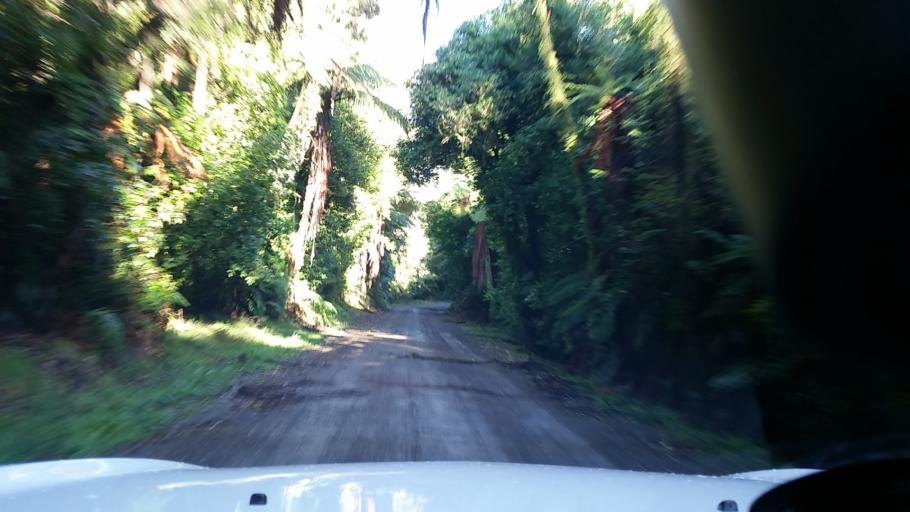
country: NZ
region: Bay of Plenty
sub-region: Kawerau District
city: Kawerau
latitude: -38.0199
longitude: 176.5775
